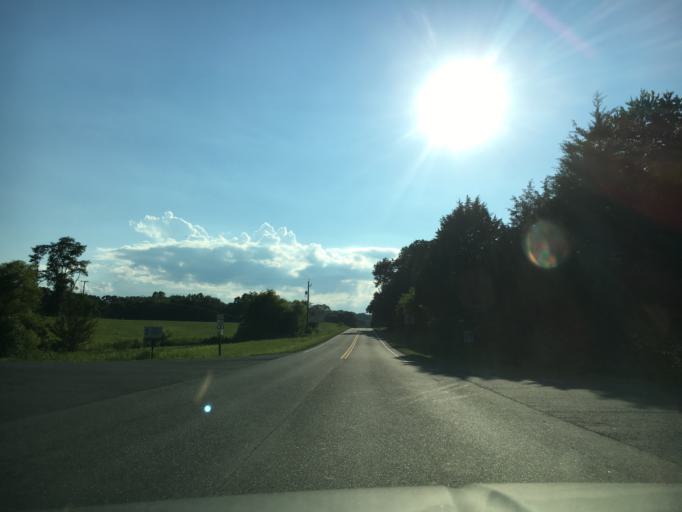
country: US
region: Virginia
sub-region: Franklin County
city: North Shore
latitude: 37.2400
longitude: -79.6551
